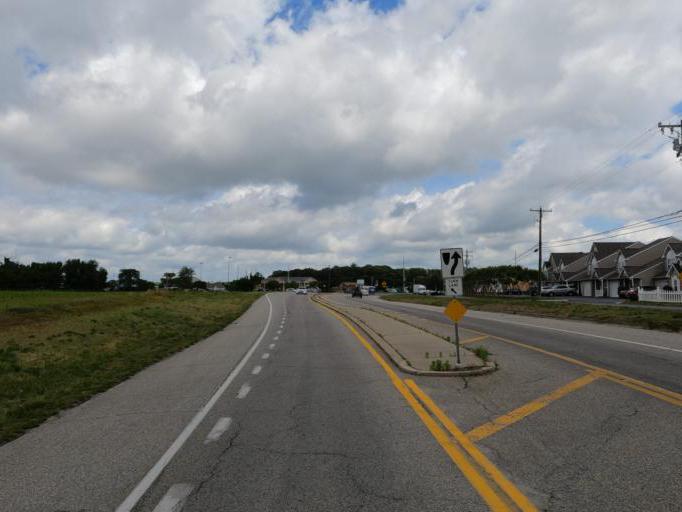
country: US
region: Delaware
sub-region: Sussex County
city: Lewes
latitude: 38.7256
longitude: -75.1304
